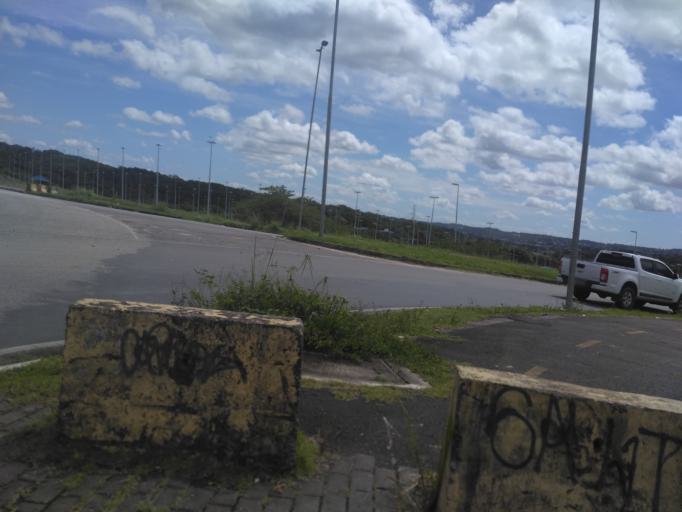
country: BR
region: Pernambuco
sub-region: Sao Lourenco Da Mata
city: Sao Lourenco da Mata
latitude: -8.0449
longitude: -35.0107
